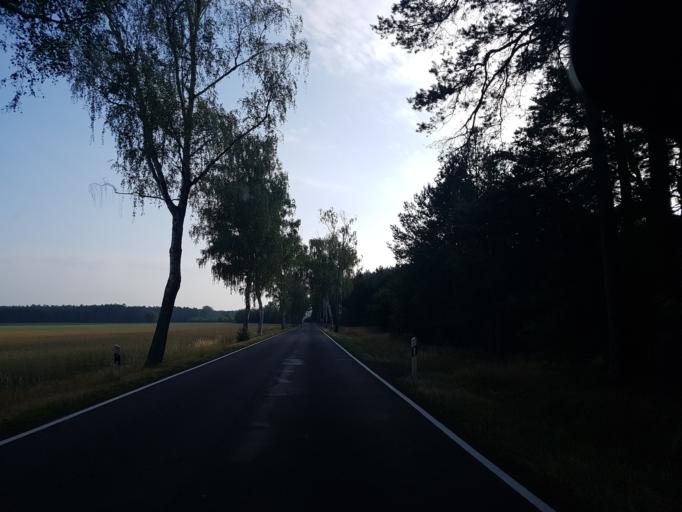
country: DE
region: Brandenburg
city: Schlieben
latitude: 51.7498
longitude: 13.3433
